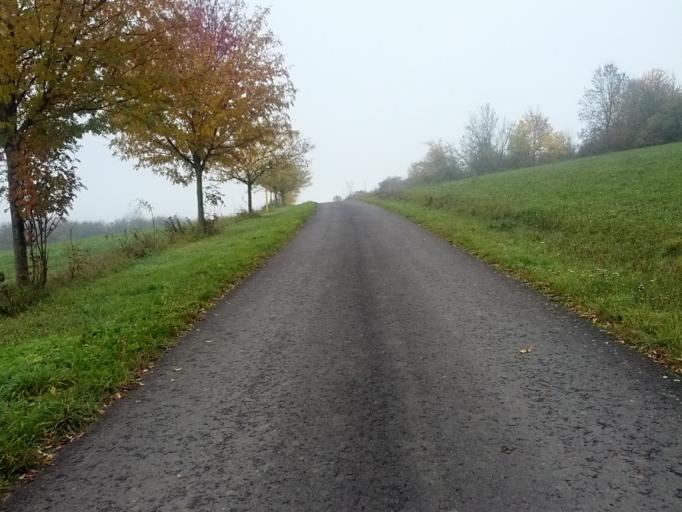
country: DE
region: Thuringia
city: Thal
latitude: 50.9711
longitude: 10.3733
